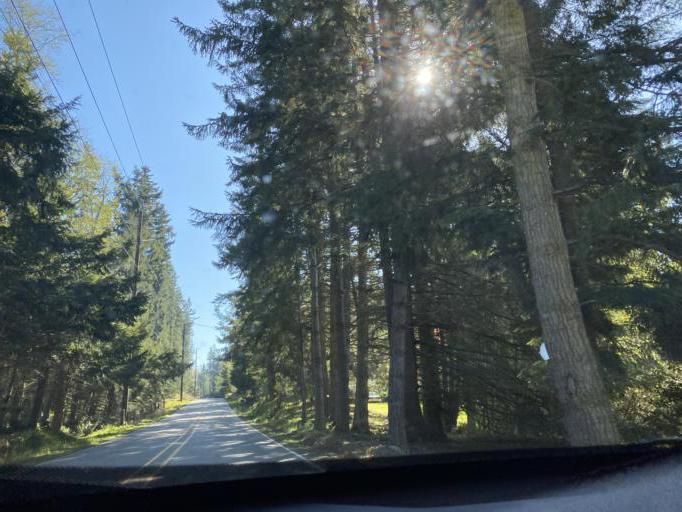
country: US
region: Washington
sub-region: Island County
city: Freeland
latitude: 48.0799
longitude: -122.5883
